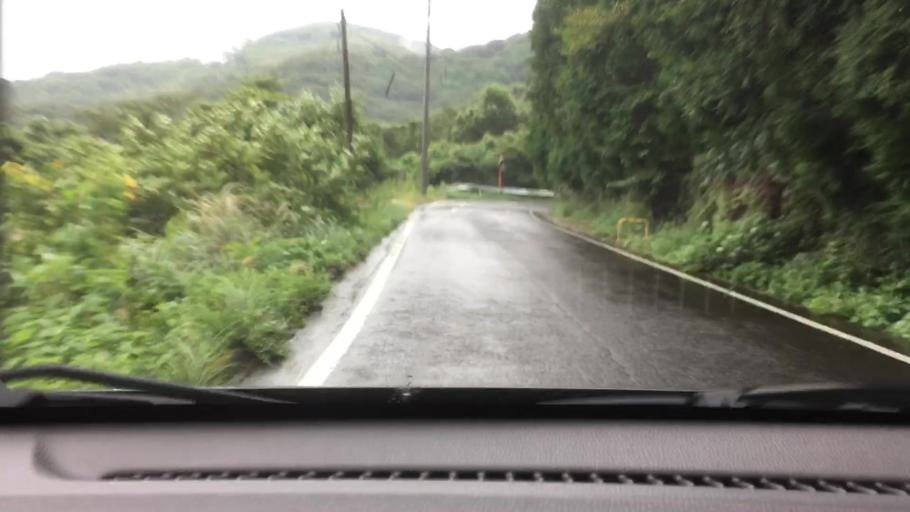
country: JP
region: Nagasaki
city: Togitsu
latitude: 32.8766
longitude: 129.7599
